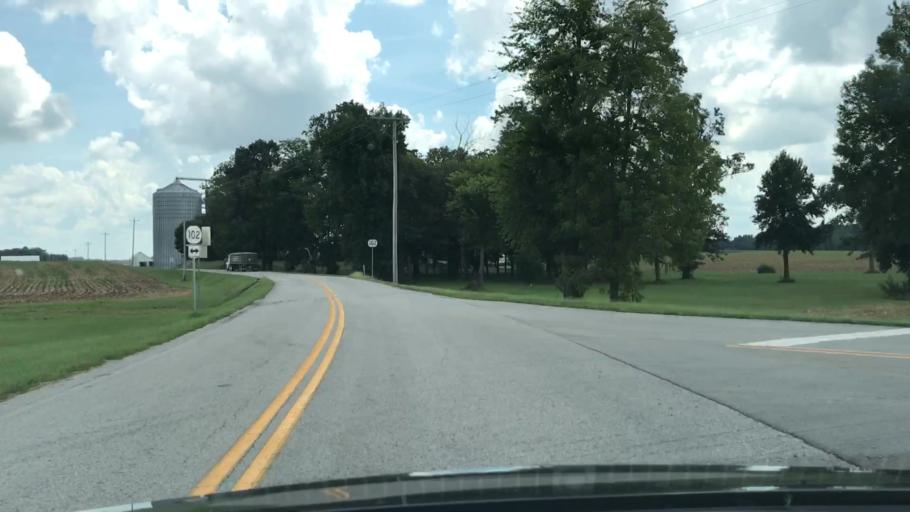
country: US
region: Kentucky
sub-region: Todd County
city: Guthrie
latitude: 36.6560
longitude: -87.0253
